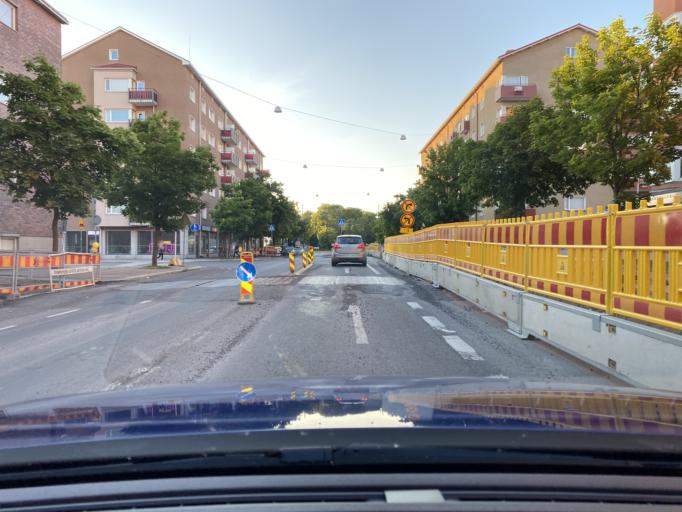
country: FI
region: Pirkanmaa
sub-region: Tampere
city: Tampere
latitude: 61.5015
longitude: 23.7869
